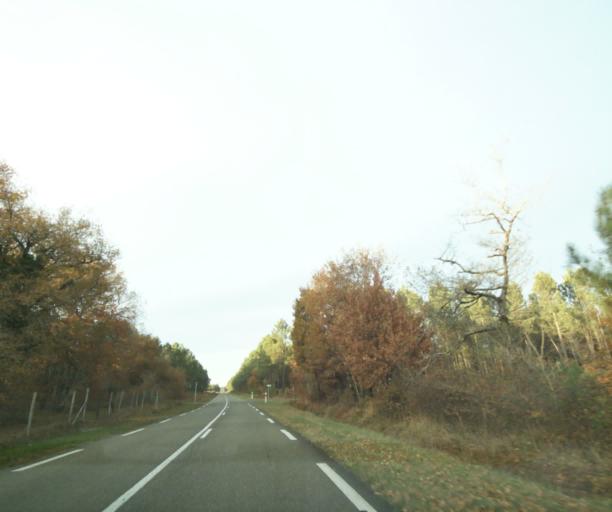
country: FR
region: Aquitaine
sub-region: Departement des Landes
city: Gabarret
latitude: 44.1550
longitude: -0.1306
